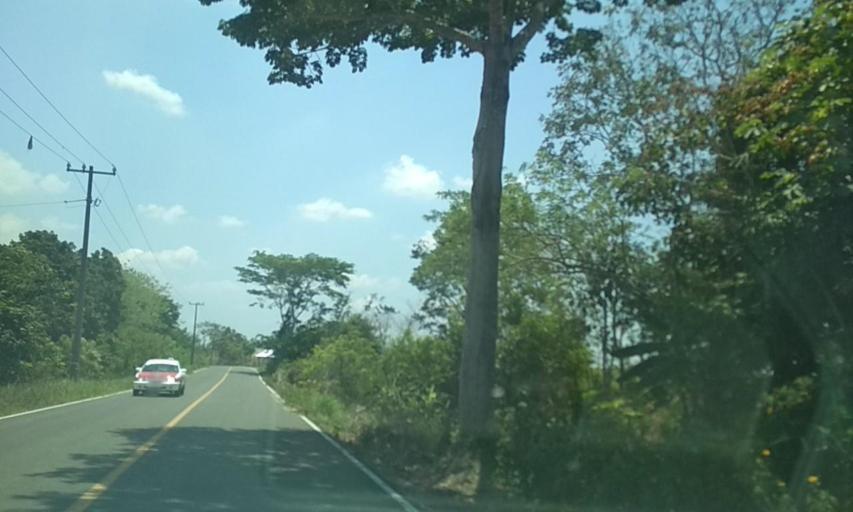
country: MX
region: Tabasco
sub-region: Huimanguillo
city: Francisco Rueda
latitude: 17.7647
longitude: -94.0592
